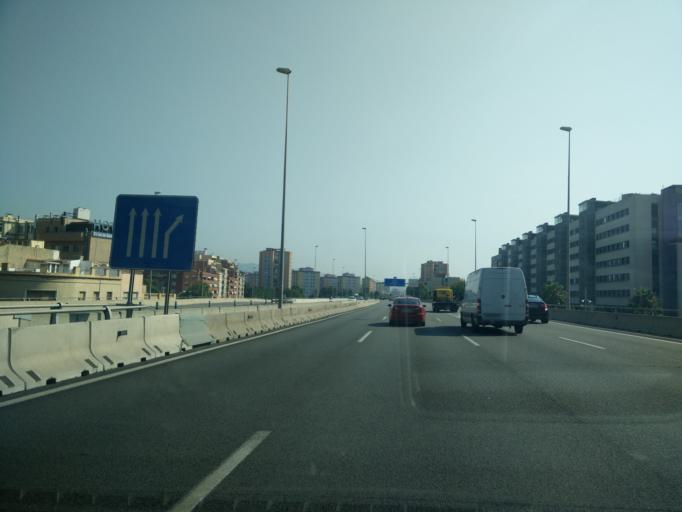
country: ES
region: Catalonia
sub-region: Provincia de Barcelona
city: Sant Adria de Besos
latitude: 41.4289
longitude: 2.2209
